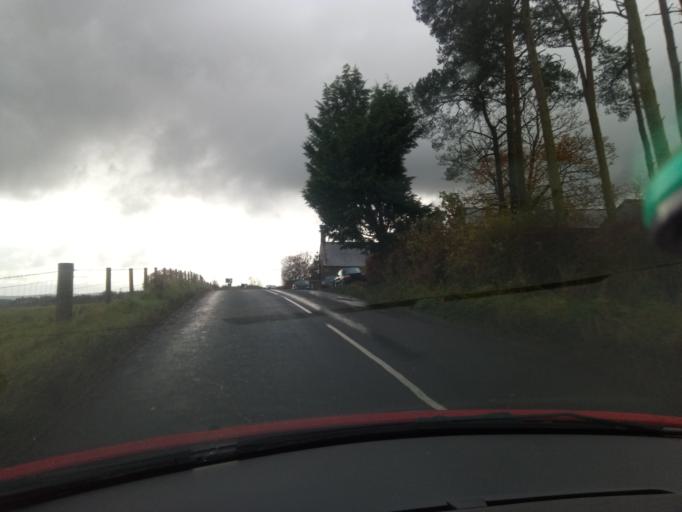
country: GB
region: England
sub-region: Northumberland
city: Birtley
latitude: 55.1131
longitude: -2.2404
